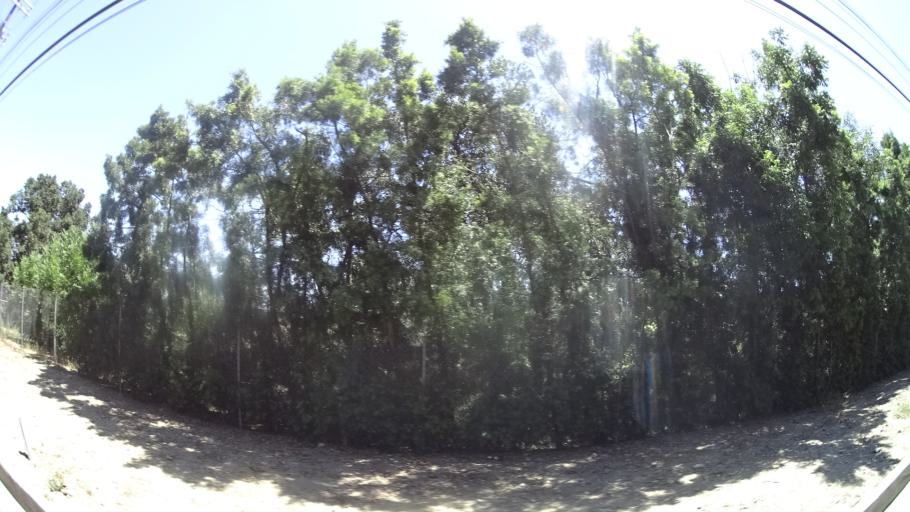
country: US
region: California
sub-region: Los Angeles County
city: Sherman Oaks
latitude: 34.1327
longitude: -118.4480
